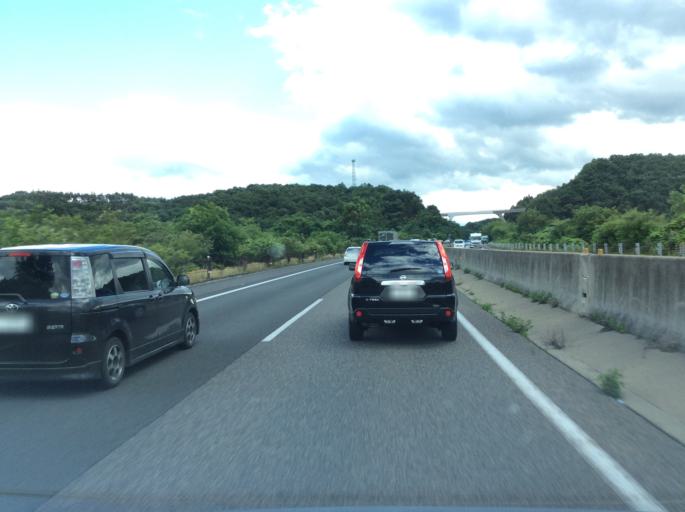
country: JP
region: Fukushima
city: Nihommatsu
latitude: 37.6416
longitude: 140.4347
